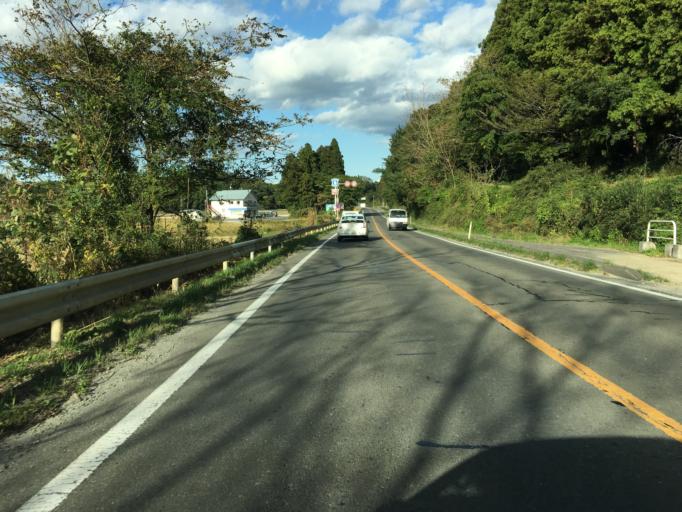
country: JP
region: Miyagi
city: Marumori
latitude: 37.9084
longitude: 140.9019
